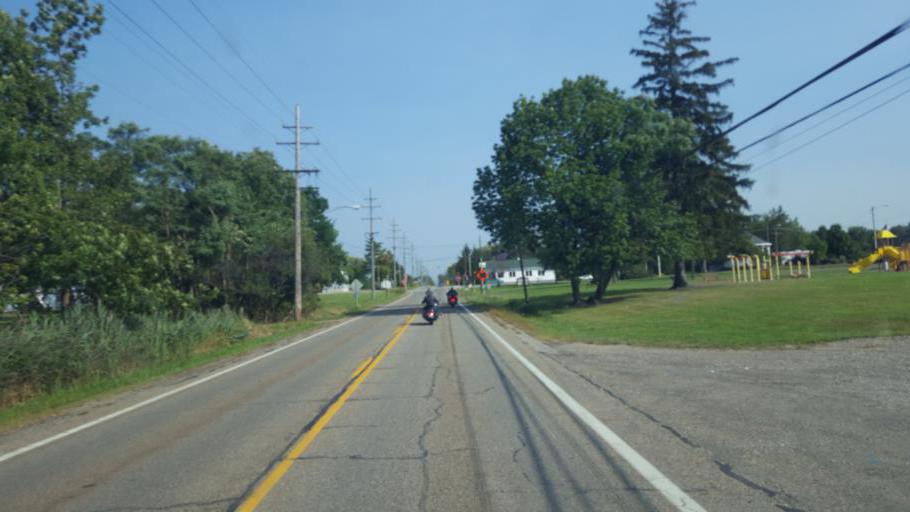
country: US
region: Ohio
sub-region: Ashtabula County
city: Roaming Shores
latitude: 41.6039
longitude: -80.8650
